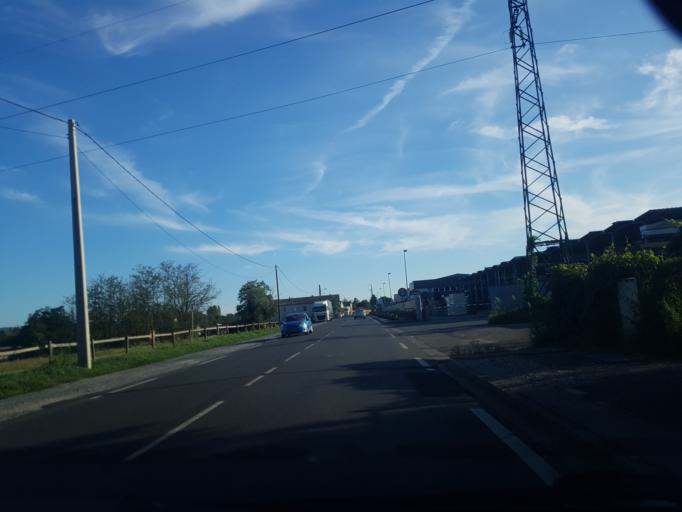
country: FR
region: Rhone-Alpes
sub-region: Departement du Rhone
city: Villefranche-sur-Saone
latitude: 45.9757
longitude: 4.7288
